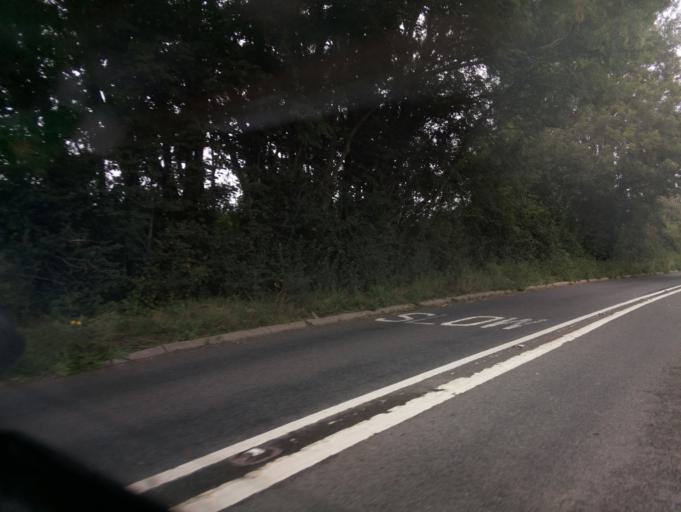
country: GB
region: England
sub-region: Devon
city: Cullompton
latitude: 50.8747
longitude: -3.3871
